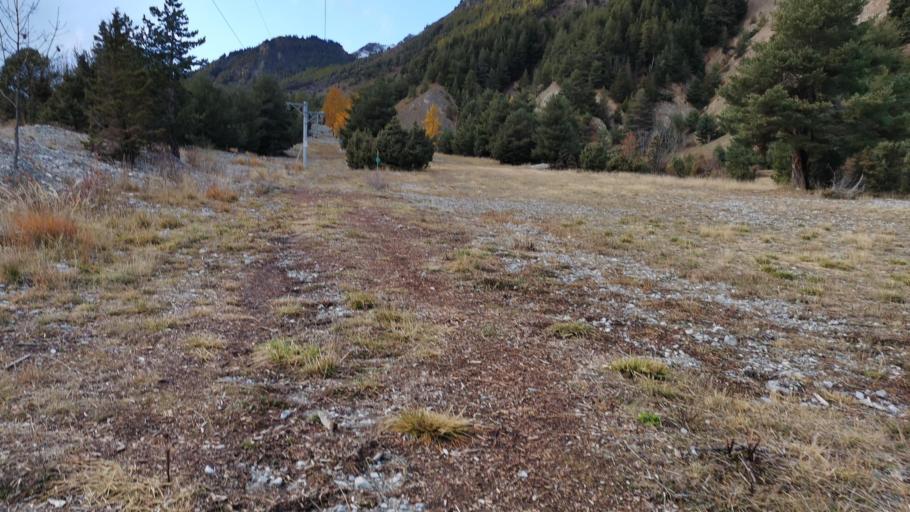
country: IT
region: Piedmont
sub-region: Provincia di Torino
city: Bardonecchia
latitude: 45.0216
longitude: 6.6270
